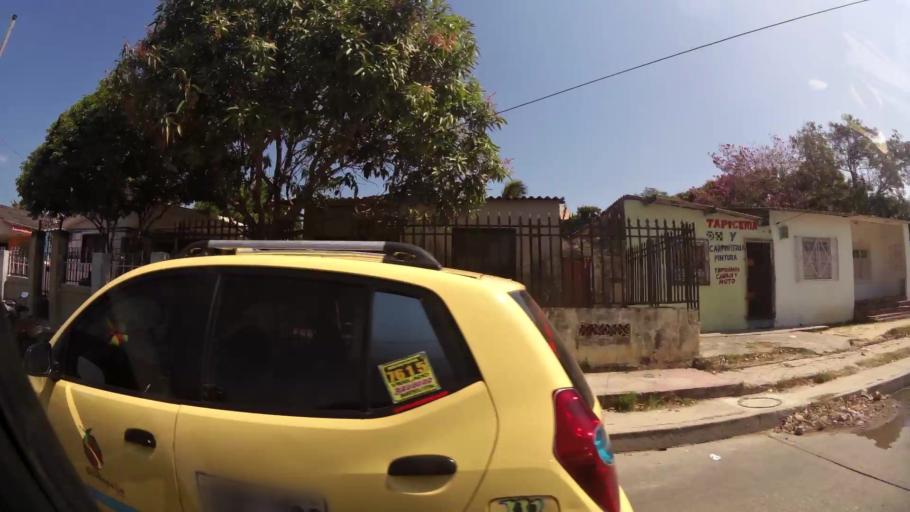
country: CO
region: Atlantico
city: Barranquilla
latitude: 10.9719
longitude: -74.8233
